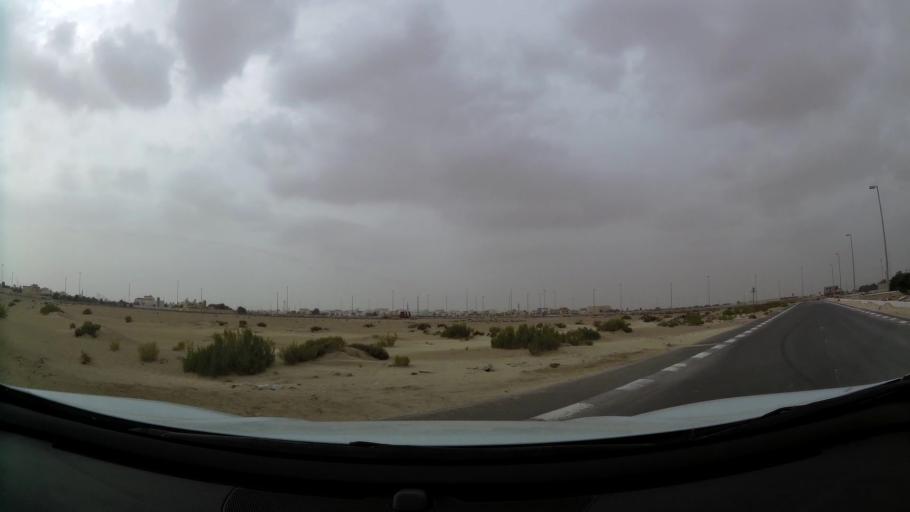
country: AE
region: Abu Dhabi
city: Abu Dhabi
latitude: 24.3659
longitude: 54.6638
